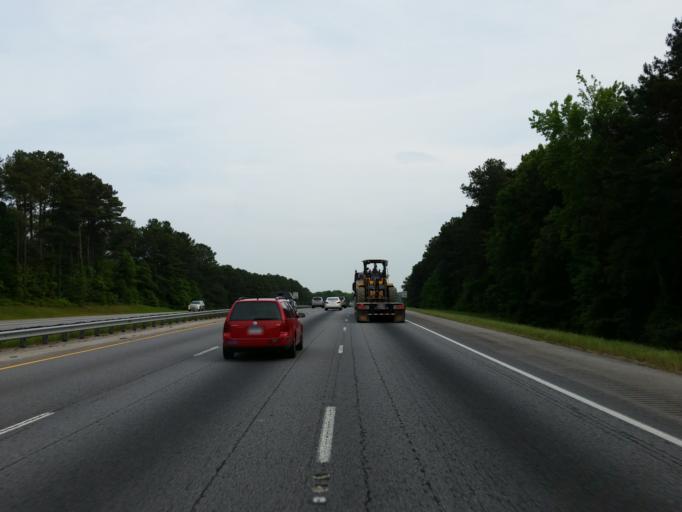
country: US
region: Georgia
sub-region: Henry County
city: Locust Grove
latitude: 33.3102
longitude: -84.1161
